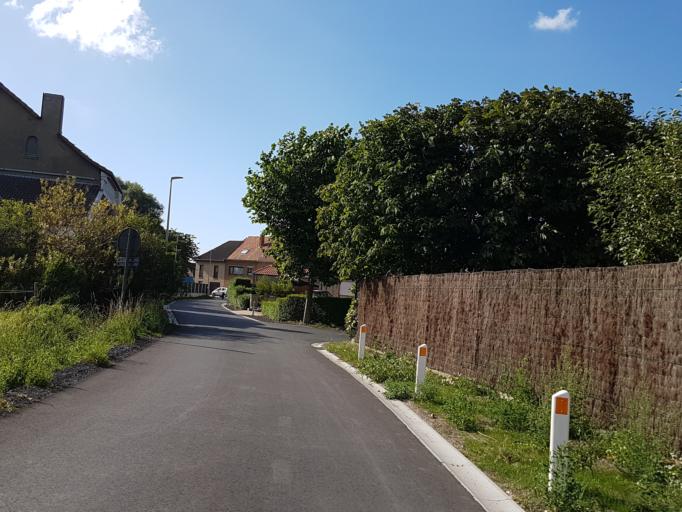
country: BE
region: Flanders
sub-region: Provincie West-Vlaanderen
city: Bredene
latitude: 51.2378
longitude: 2.9666
